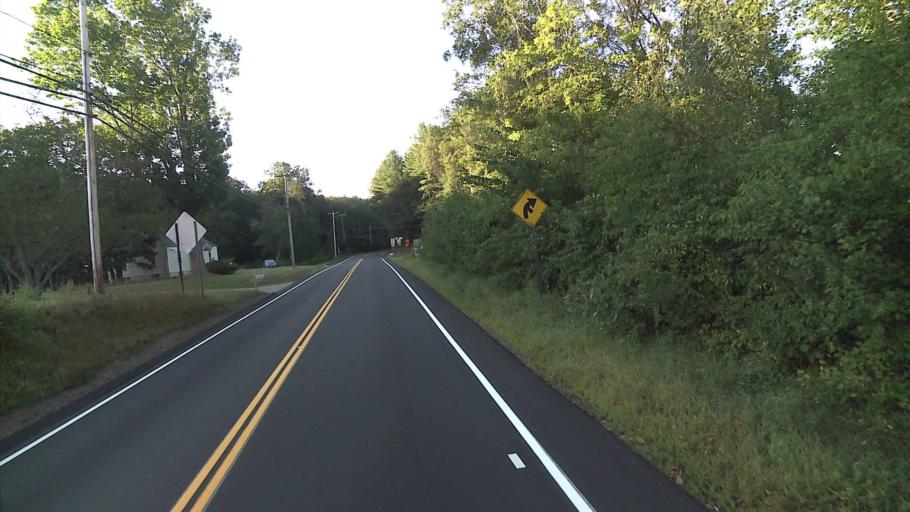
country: US
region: Connecticut
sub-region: Tolland County
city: Tolland
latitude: 41.8802
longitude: -72.3016
